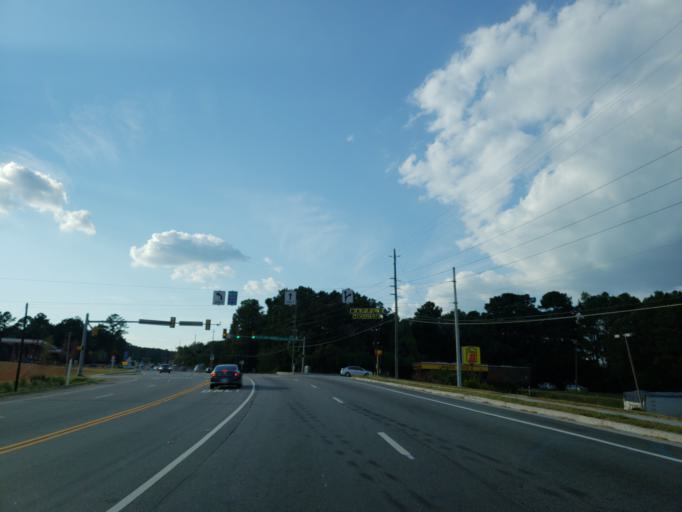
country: US
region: Georgia
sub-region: Cobb County
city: Mableton
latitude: 33.7753
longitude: -84.5613
